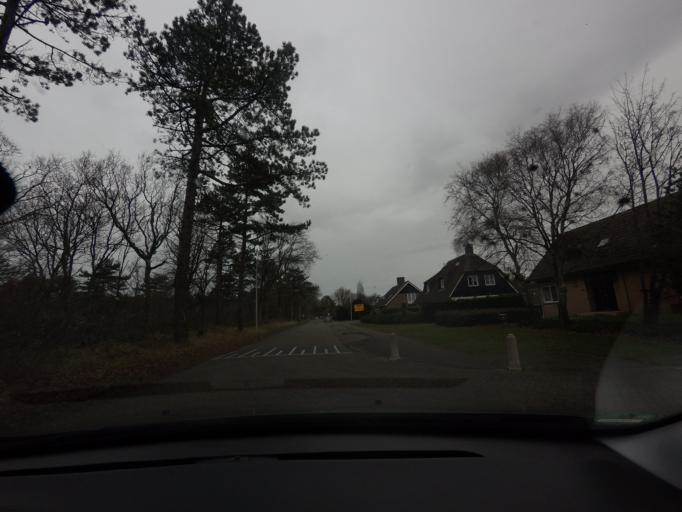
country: NL
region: North Holland
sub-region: Gemeente Texel
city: Den Burg
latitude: 53.0923
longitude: 4.7581
